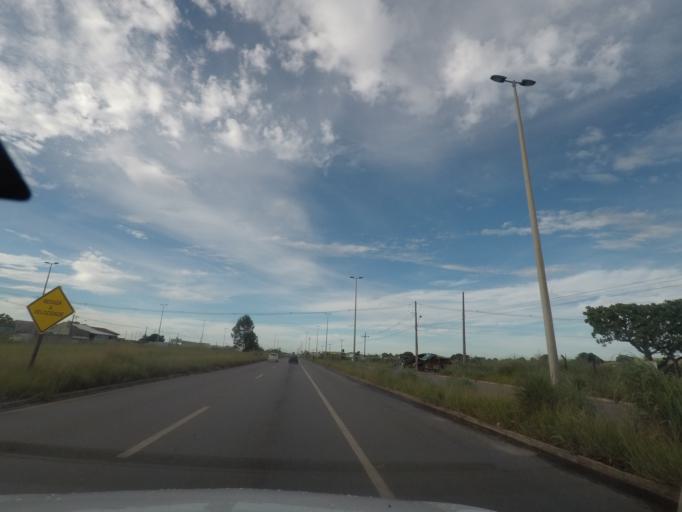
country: BR
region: Goias
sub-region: Aparecida De Goiania
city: Aparecida de Goiania
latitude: -16.7761
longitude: -49.3524
